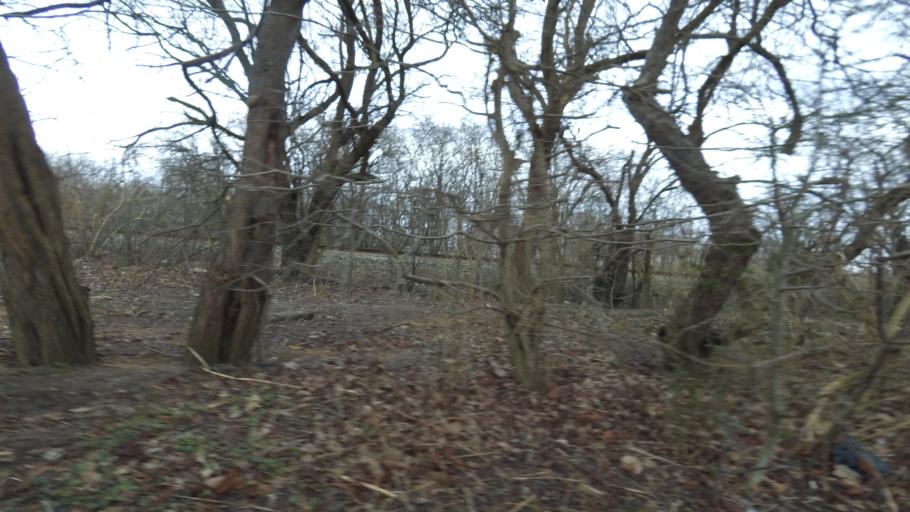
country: DK
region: Central Jutland
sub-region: Arhus Kommune
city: Tranbjerg
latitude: 56.0944
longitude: 10.1400
